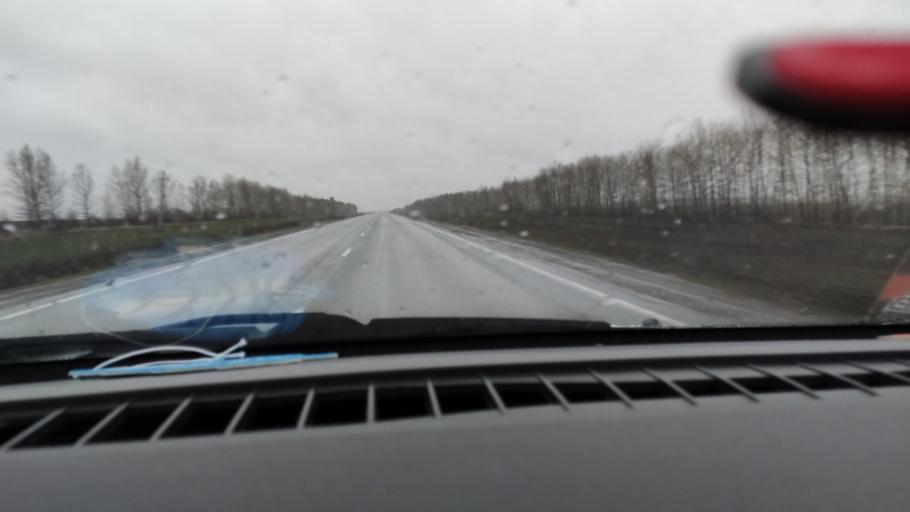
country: RU
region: Tatarstan
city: Mendeleyevsk
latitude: 55.9332
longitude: 52.2841
